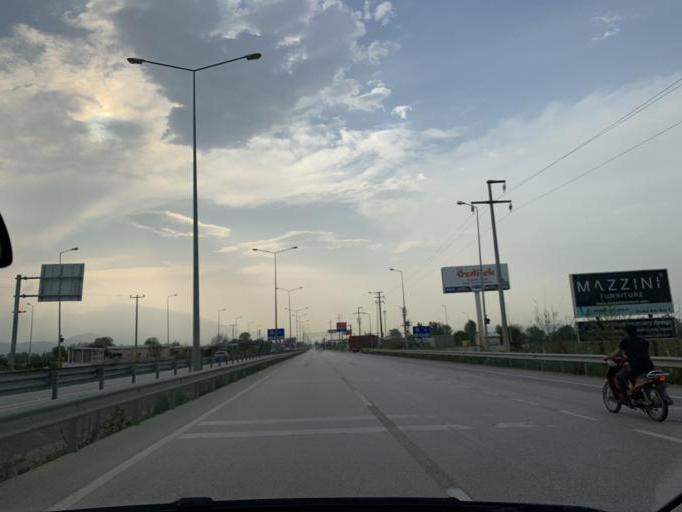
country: TR
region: Bursa
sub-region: Inegoel
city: Inegol
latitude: 40.0661
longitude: 29.5632
